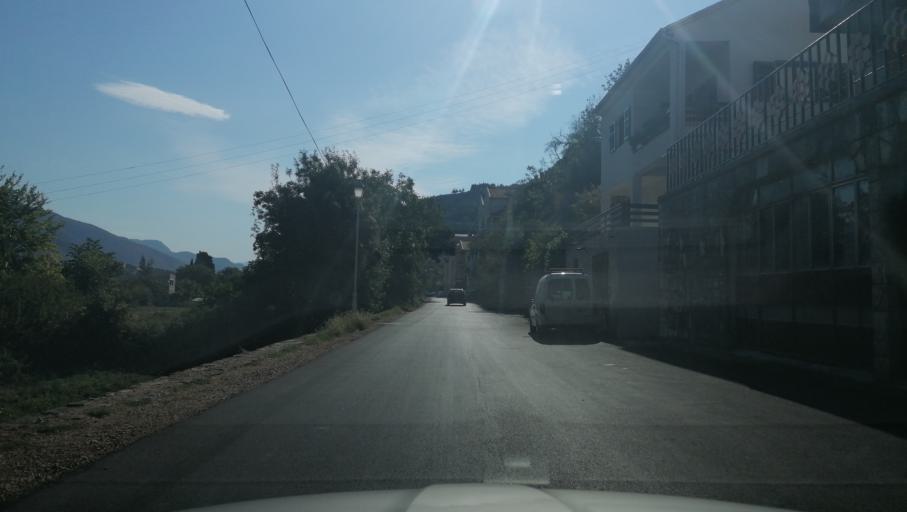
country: BA
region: Republika Srpska
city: Trebinje
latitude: 42.7142
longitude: 18.3515
